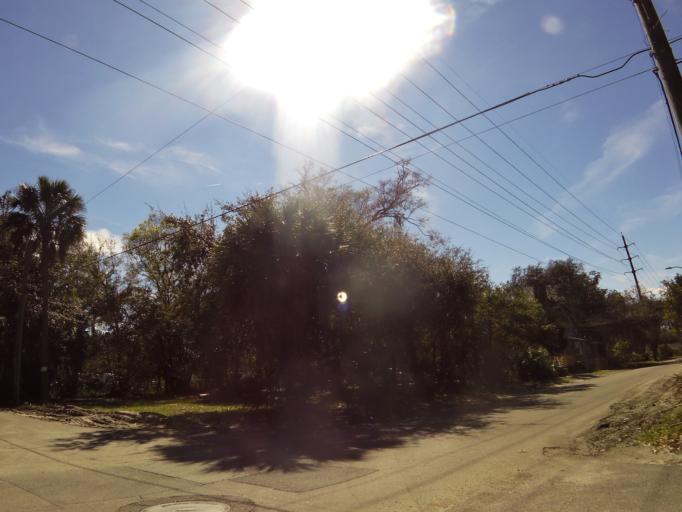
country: US
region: Florida
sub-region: Duval County
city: Jacksonville
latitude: 30.3610
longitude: -81.6461
